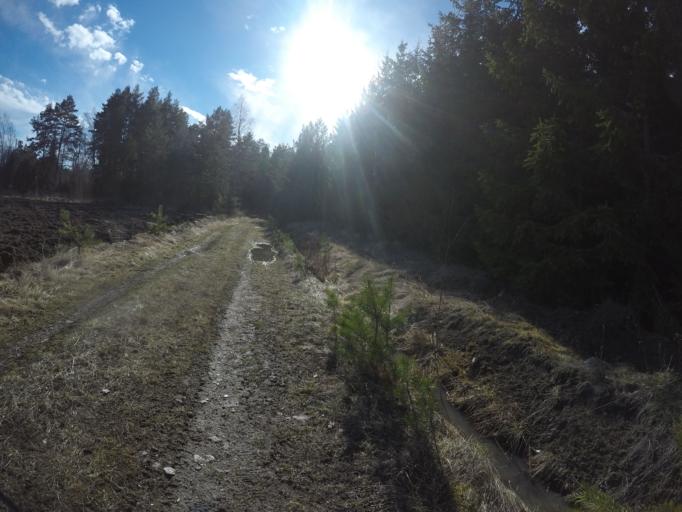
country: SE
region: Soedermanland
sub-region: Eskilstuna Kommun
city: Kvicksund
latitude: 59.4255
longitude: 16.2857
